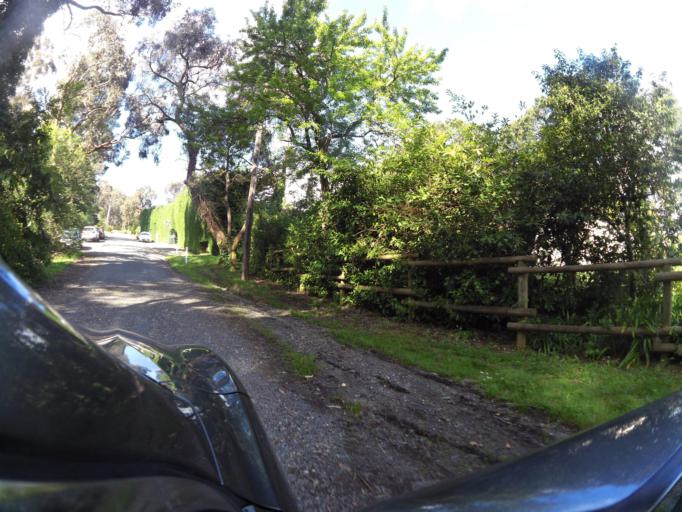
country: AU
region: Victoria
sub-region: Mount Alexander
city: Castlemaine
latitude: -37.3070
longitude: 144.1414
